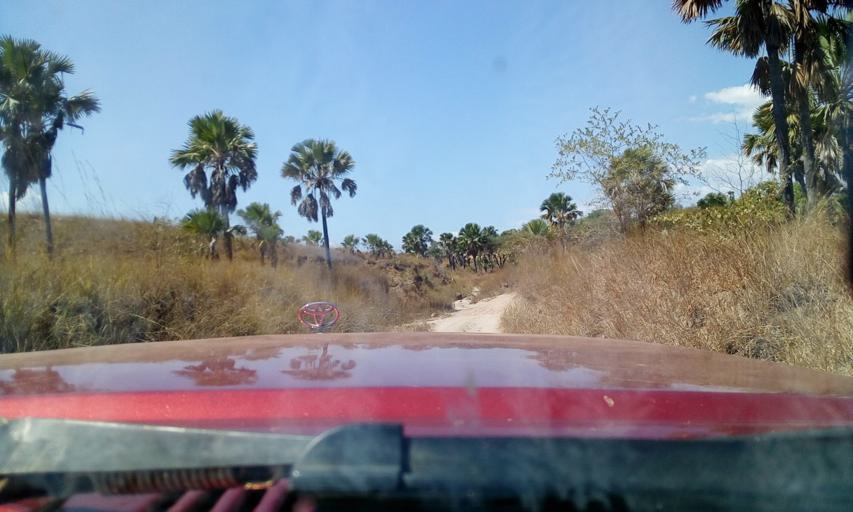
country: MG
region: Boeny
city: Sitampiky
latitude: -16.1308
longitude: 45.4969
